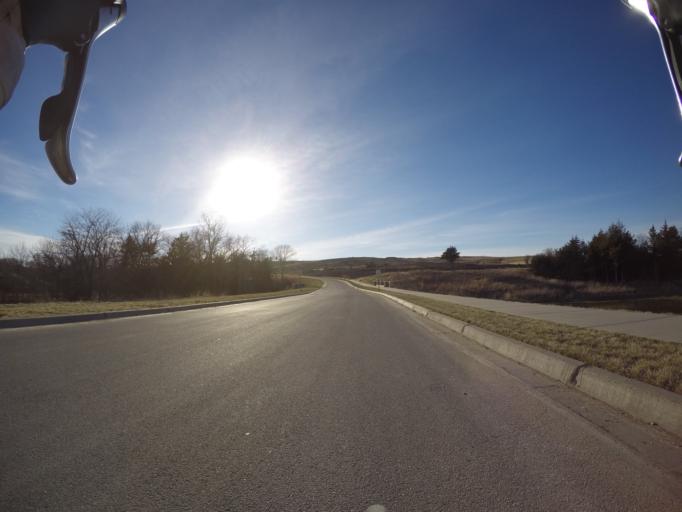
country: US
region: Kansas
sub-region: Riley County
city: Manhattan
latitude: 39.2115
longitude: -96.6336
